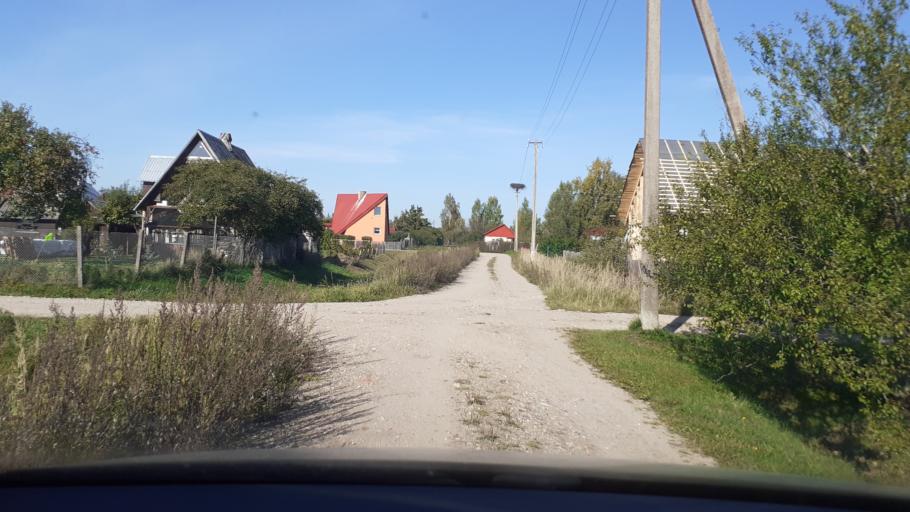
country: LV
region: Kuldigas Rajons
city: Kuldiga
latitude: 56.9496
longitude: 21.9780
